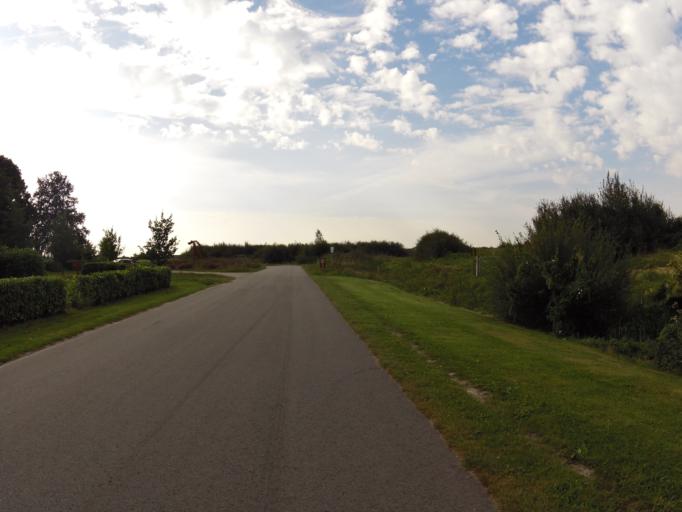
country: NL
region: Drenthe
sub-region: Gemeente Emmen
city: Klazienaveen
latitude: 52.7017
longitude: 7.0449
